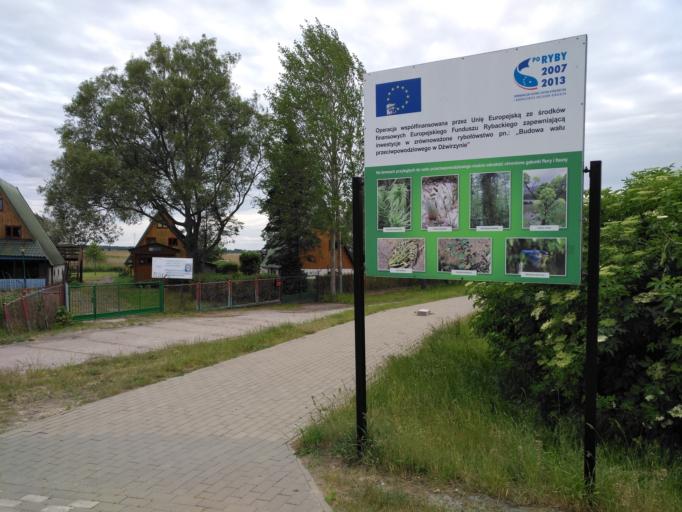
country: PL
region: West Pomeranian Voivodeship
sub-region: Powiat kolobrzeski
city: Grzybowo
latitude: 54.1524
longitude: 15.3972
